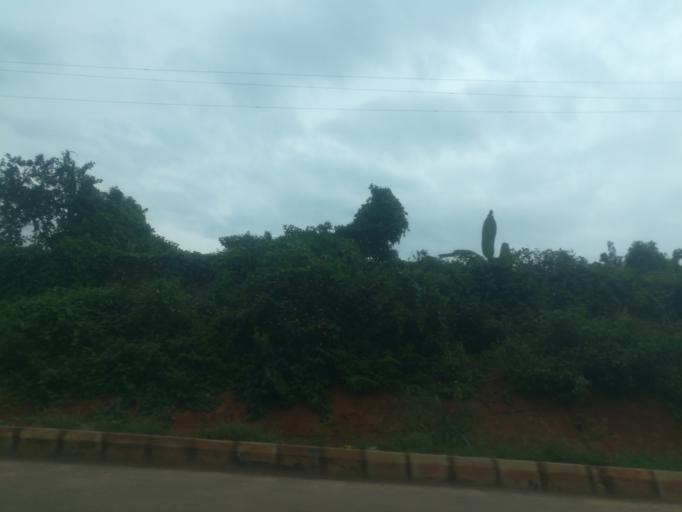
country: NG
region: Oyo
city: Ibadan
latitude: 7.3902
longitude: 3.9332
